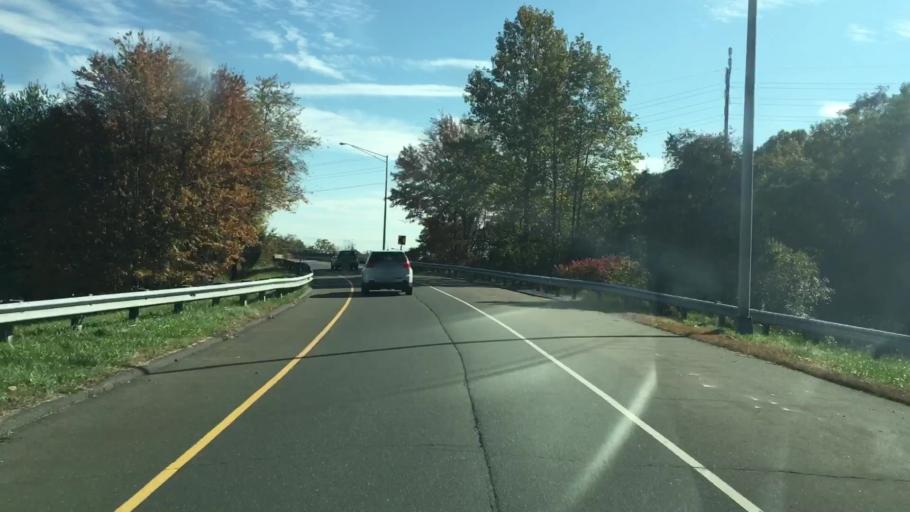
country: US
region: Connecticut
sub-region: Fairfield County
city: Trumbull
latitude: 41.2333
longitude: -73.1910
